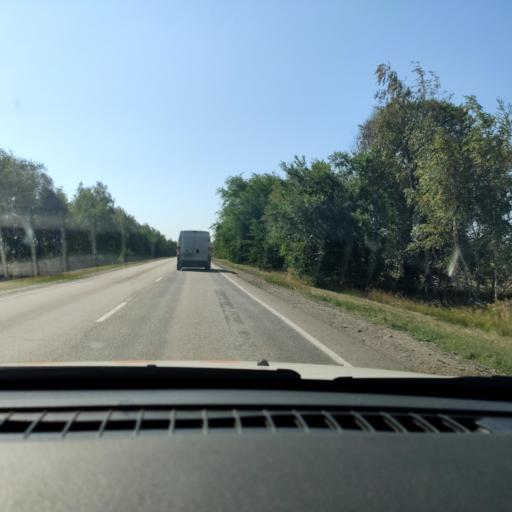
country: RU
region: Voronezj
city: Liski
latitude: 50.8018
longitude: 39.3303
